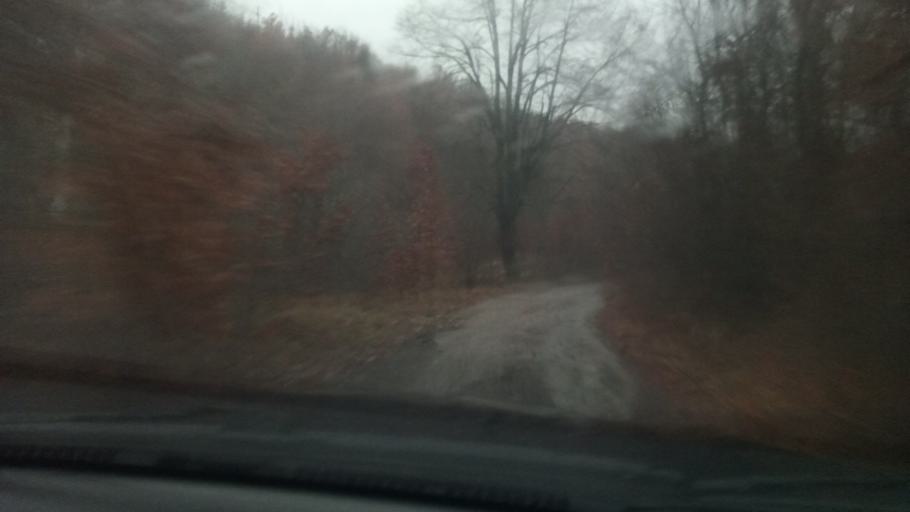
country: MK
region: Vinica
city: Blatec
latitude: 41.8387
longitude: 22.6110
